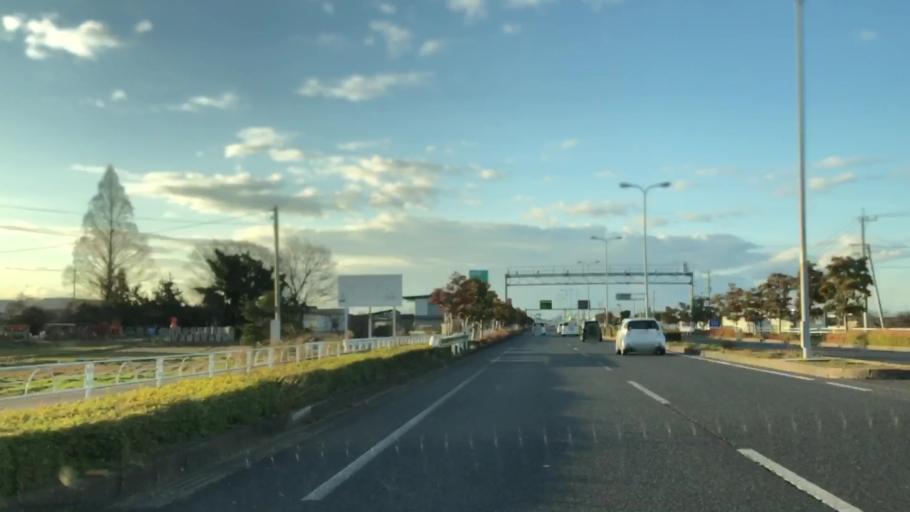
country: JP
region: Fukuoka
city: Nakatsu
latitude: 33.5448
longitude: 131.2851
